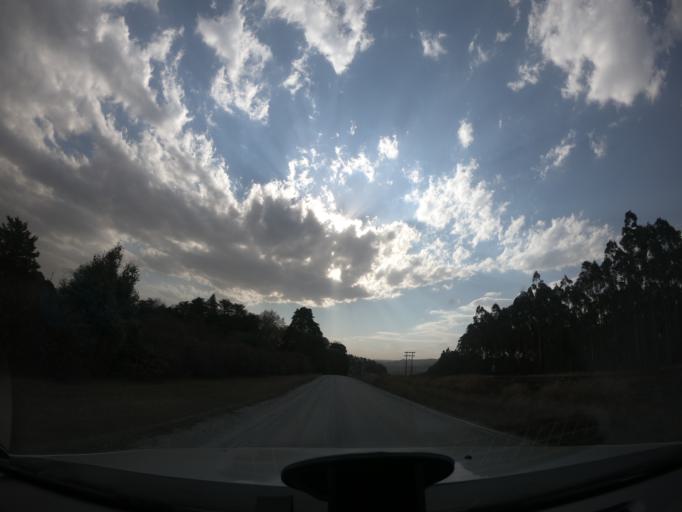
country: ZA
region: KwaZulu-Natal
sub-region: uMgungundlovu District Municipality
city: Howick
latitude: -29.4258
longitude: 30.1061
